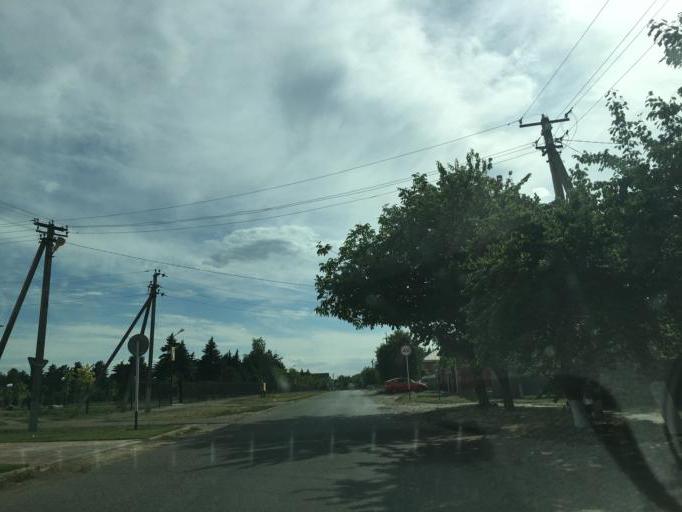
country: RU
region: Krasnodarskiy
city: Kushchevskaya
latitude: 46.5540
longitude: 39.6265
